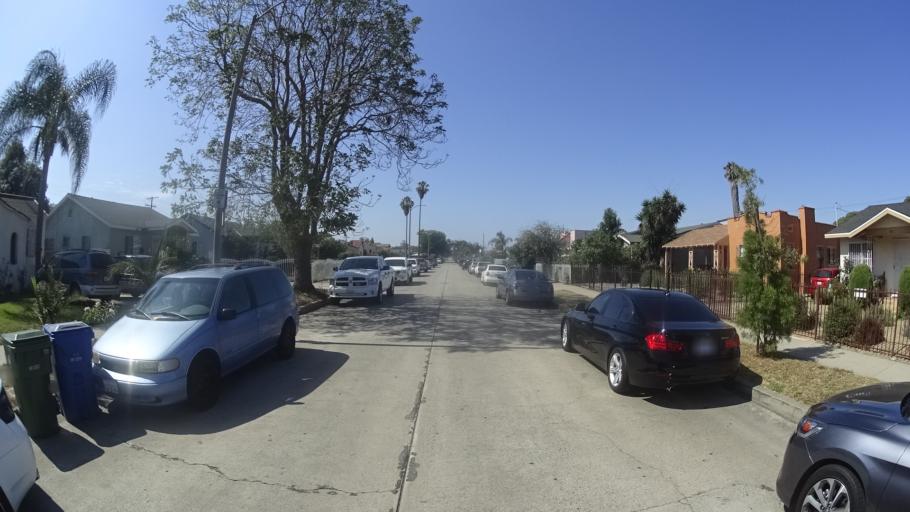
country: US
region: California
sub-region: Los Angeles County
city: View Park-Windsor Hills
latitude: 33.9793
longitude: -118.3236
